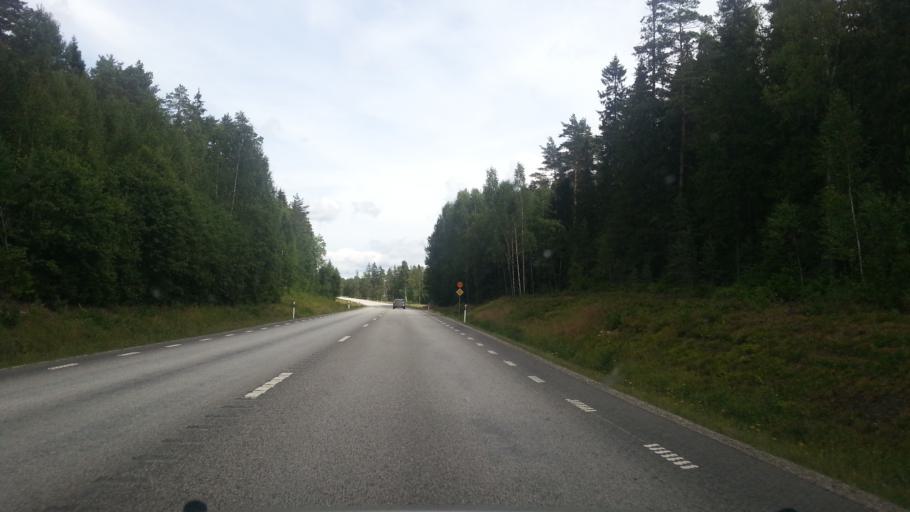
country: SE
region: OErebro
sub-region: Lindesbergs Kommun
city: Lindesberg
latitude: 59.6666
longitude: 15.2750
